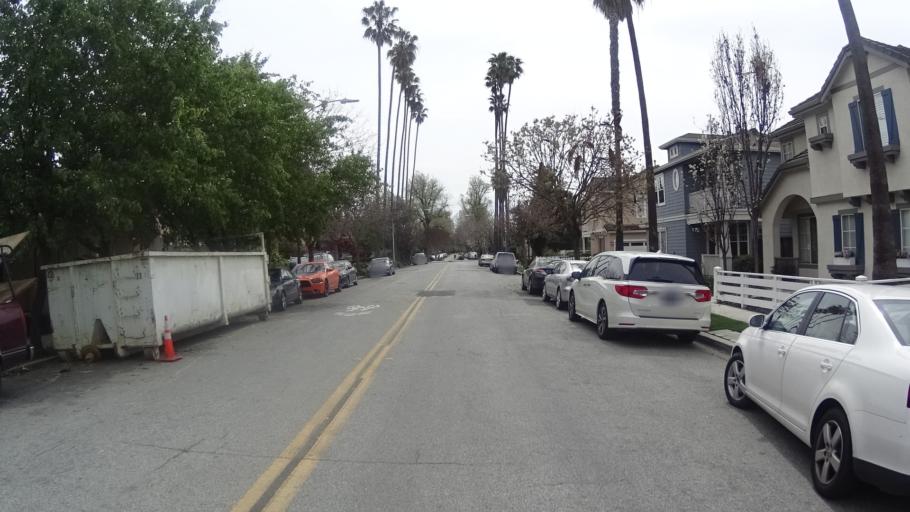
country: US
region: California
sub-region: Santa Clara County
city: San Jose
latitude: 37.3429
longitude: -121.8737
